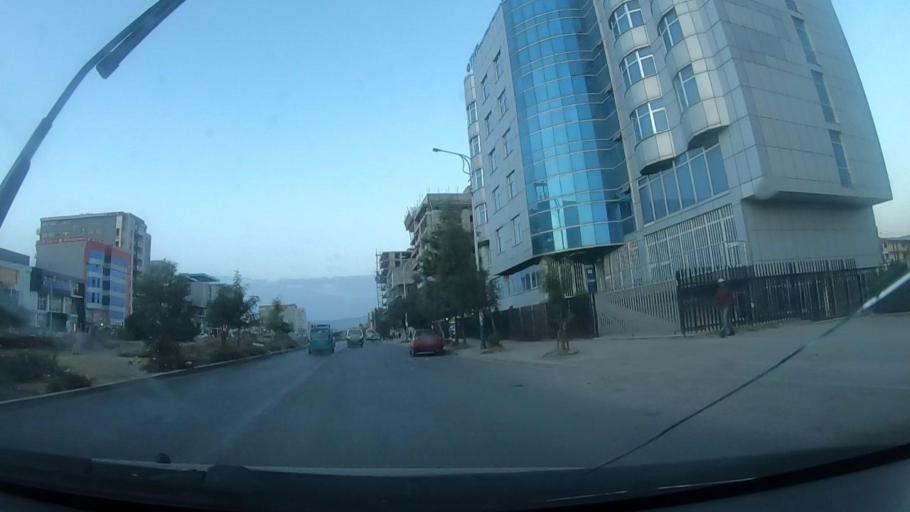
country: ET
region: Adis Abeba
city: Addis Ababa
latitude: 9.0308
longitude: 38.8780
